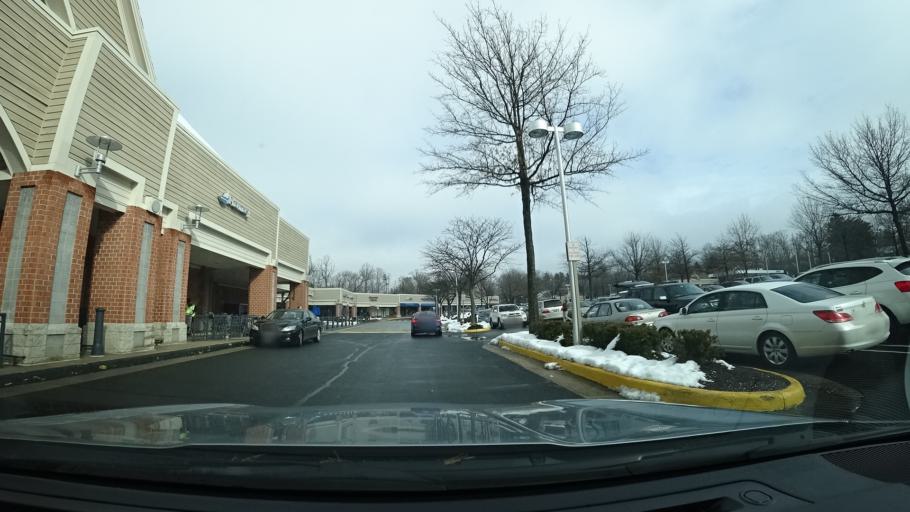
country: US
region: Virginia
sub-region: Fairfax County
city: Reston
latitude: 38.9791
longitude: -77.3499
